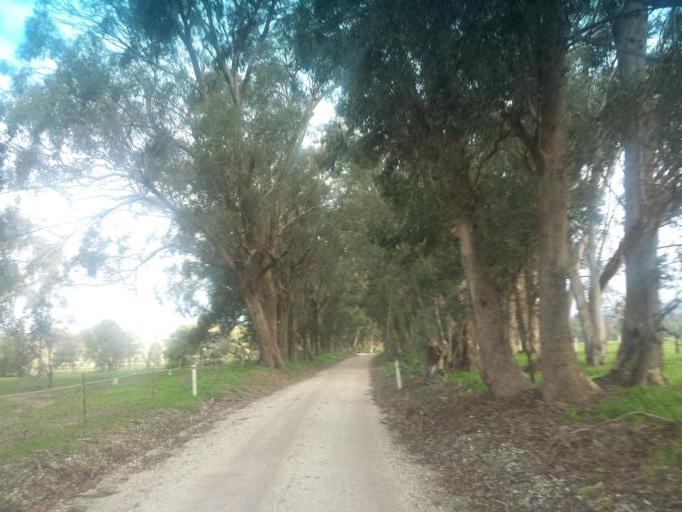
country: AU
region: Victoria
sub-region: Murrindindi
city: Kinglake West
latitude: -37.0351
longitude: 145.2319
